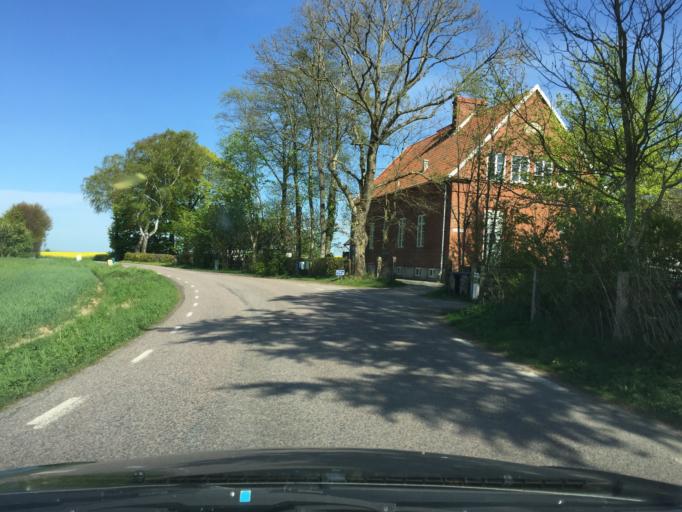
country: SE
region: Skane
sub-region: Sjobo Kommun
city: Blentarp
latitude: 55.5681
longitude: 13.5547
